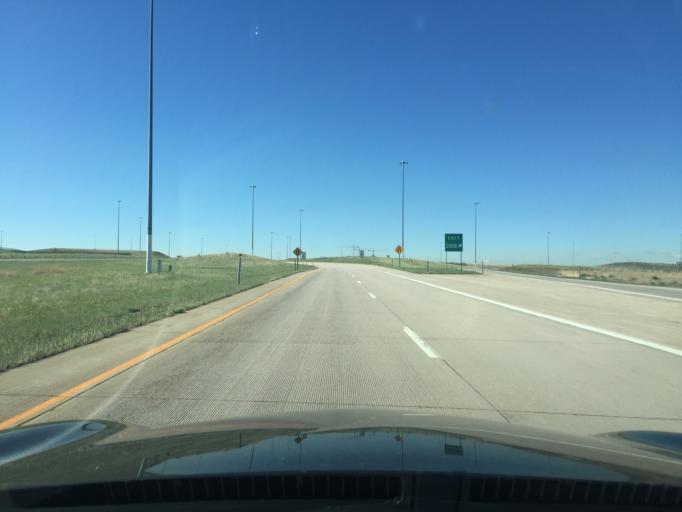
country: US
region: Colorado
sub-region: Adams County
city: Aurora
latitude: 39.8399
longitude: -104.7476
